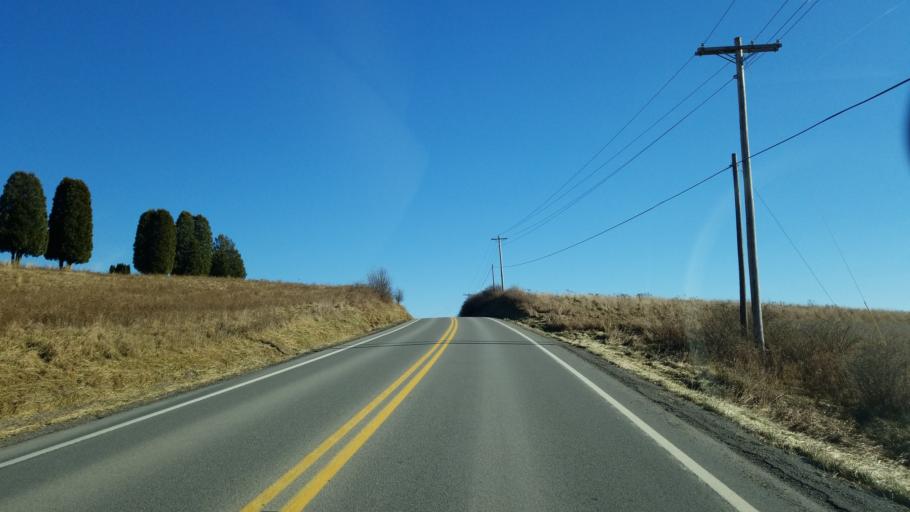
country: US
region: Pennsylvania
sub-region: Jefferson County
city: Falls Creek
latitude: 41.1784
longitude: -78.8622
